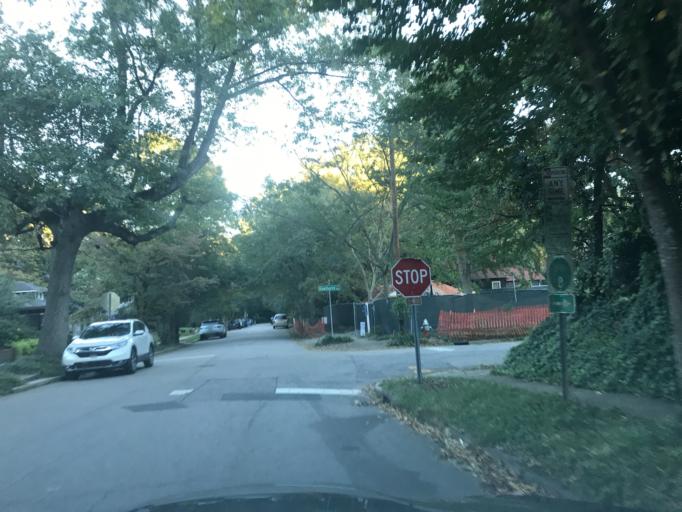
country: US
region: North Carolina
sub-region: Wake County
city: West Raleigh
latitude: 35.7881
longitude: -78.6582
